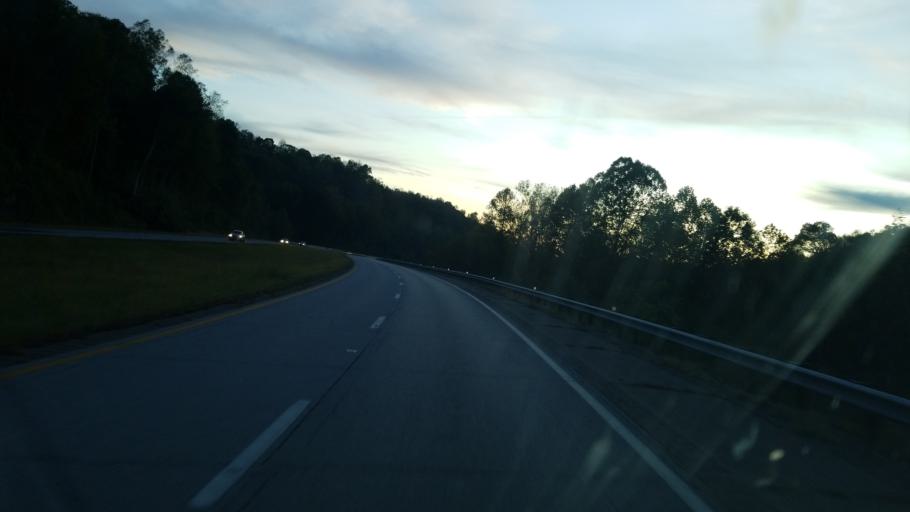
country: US
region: Ohio
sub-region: Meigs County
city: Pomeroy
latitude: 39.0546
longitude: -82.0304
